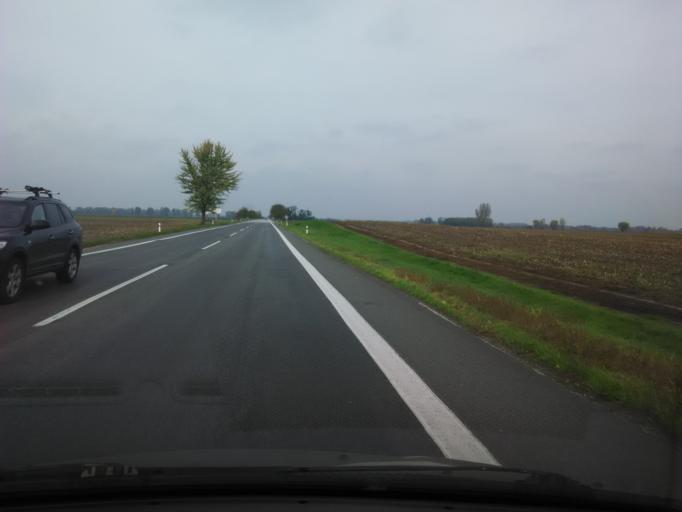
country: SK
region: Nitriansky
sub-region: Okres Komarno
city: Hurbanovo
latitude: 47.8143
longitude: 18.1824
